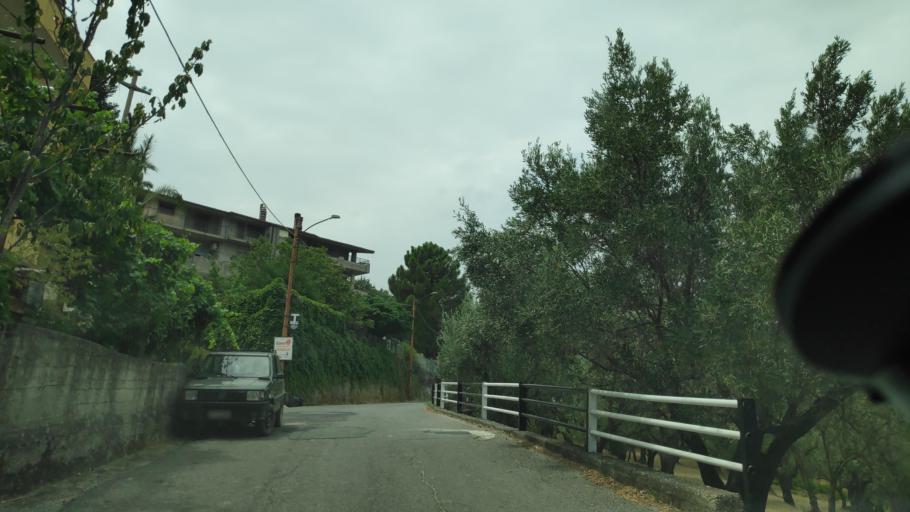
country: IT
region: Calabria
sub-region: Provincia di Catanzaro
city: Davoli
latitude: 38.6492
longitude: 16.4889
